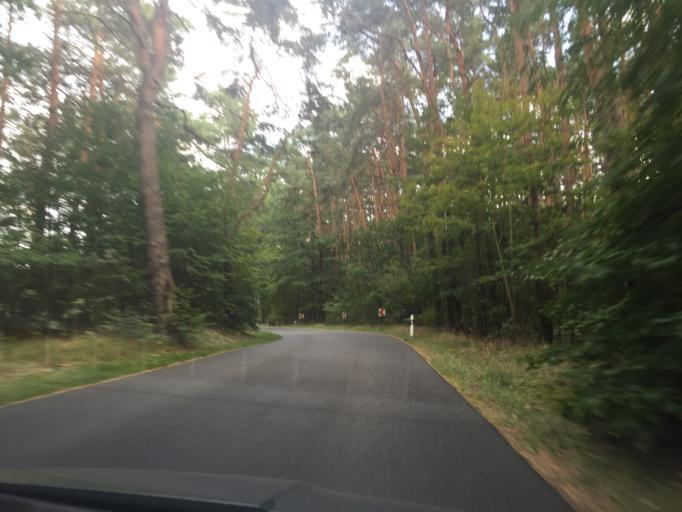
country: DE
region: Brandenburg
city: Spreenhagen
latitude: 52.3453
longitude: 13.8367
